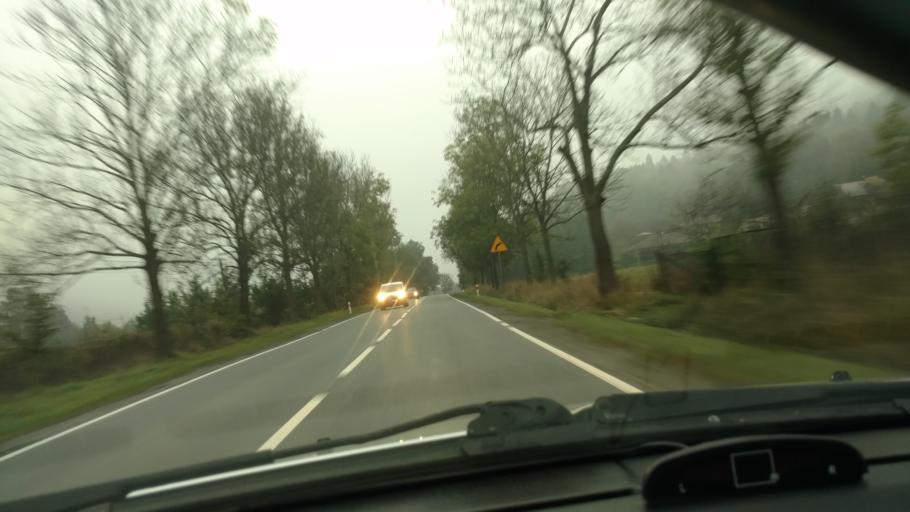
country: PL
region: Subcarpathian Voivodeship
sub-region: Powiat strzyzowski
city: Frysztak
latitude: 49.8583
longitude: 21.6238
